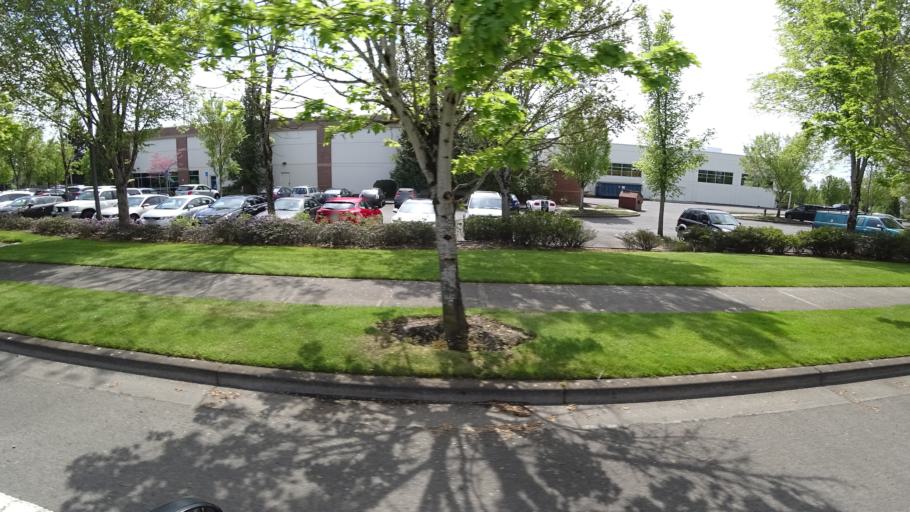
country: US
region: Oregon
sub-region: Washington County
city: Rockcreek
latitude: 45.5643
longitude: -122.8969
